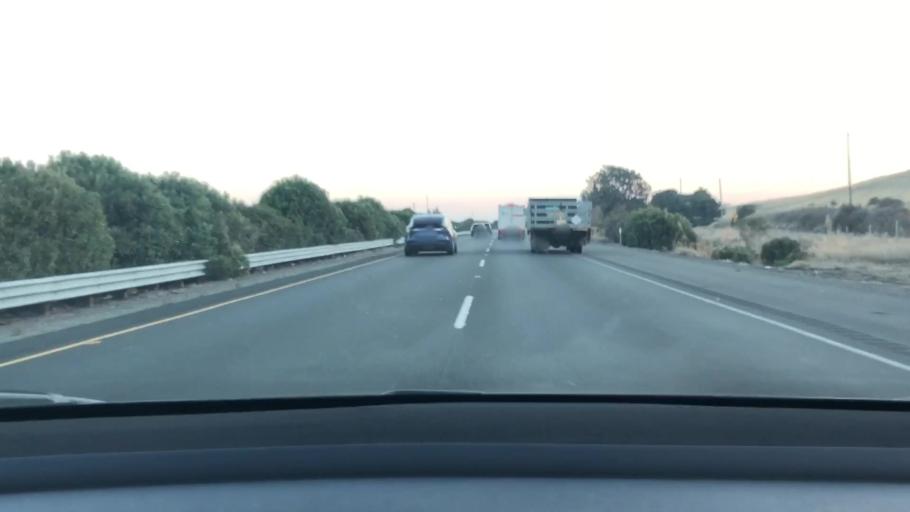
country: US
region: California
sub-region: Solano County
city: Green Valley
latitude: 38.1588
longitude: -122.1166
